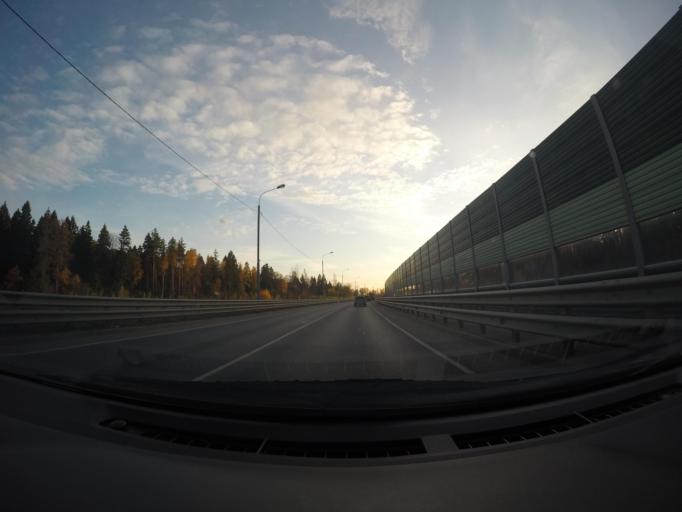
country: RU
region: Moskovskaya
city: Firsanovka
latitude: 55.9524
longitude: 37.2569
